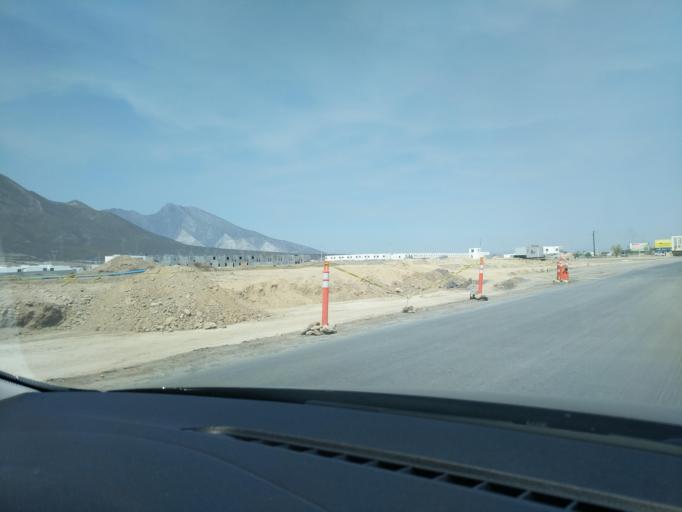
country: MX
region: Nuevo Leon
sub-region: Garcia
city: Valle de Lincoln
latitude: 25.7932
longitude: -100.4733
